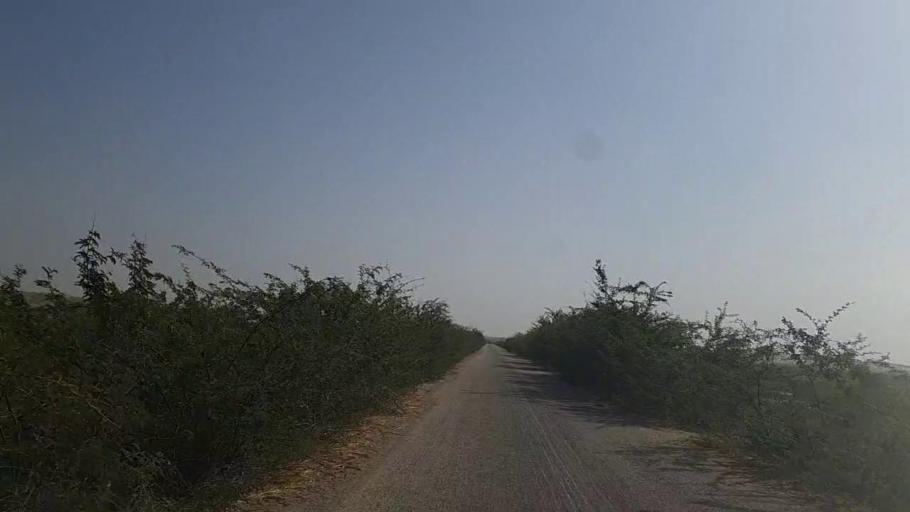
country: PK
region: Sindh
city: Kadhan
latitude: 24.5584
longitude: 69.2763
